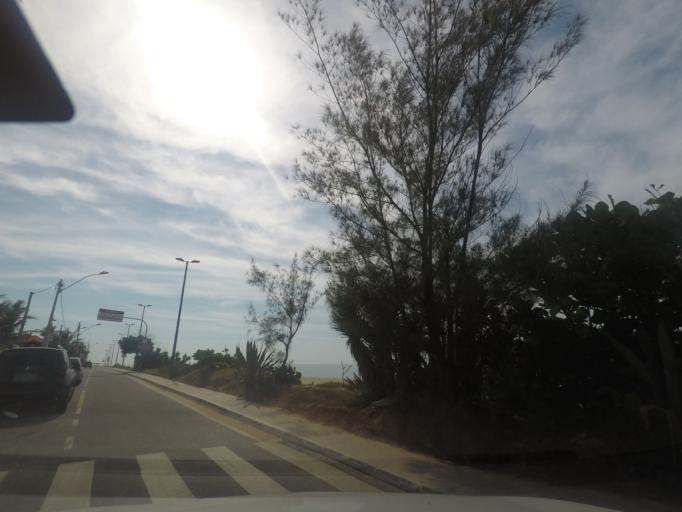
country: BR
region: Rio de Janeiro
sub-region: Marica
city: Marica
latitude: -22.9614
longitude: -42.8255
